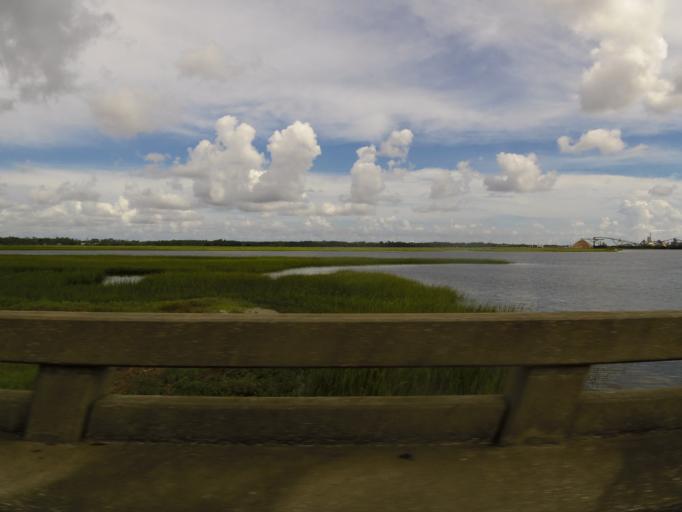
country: US
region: Georgia
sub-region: Glynn County
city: Dock Junction
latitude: 31.1916
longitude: -81.5286
